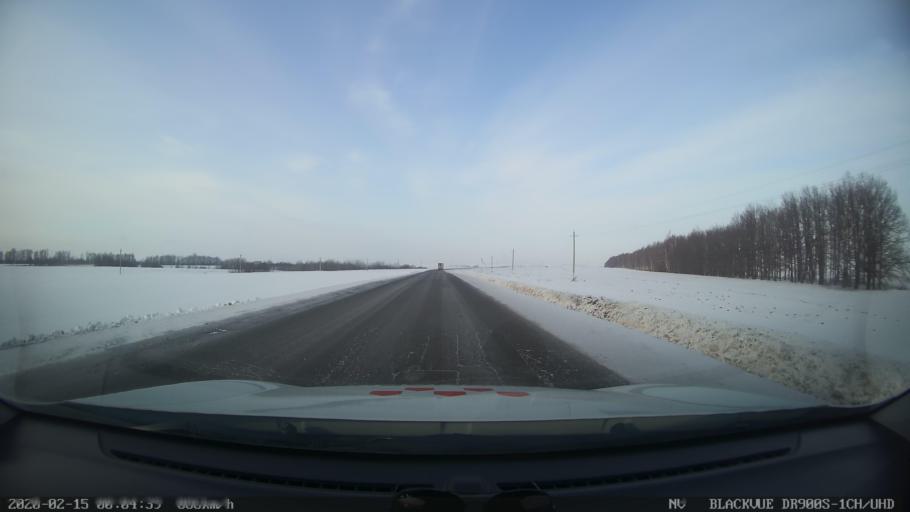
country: RU
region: Tatarstan
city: Kuybyshevskiy Zaton
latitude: 55.3848
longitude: 48.9815
